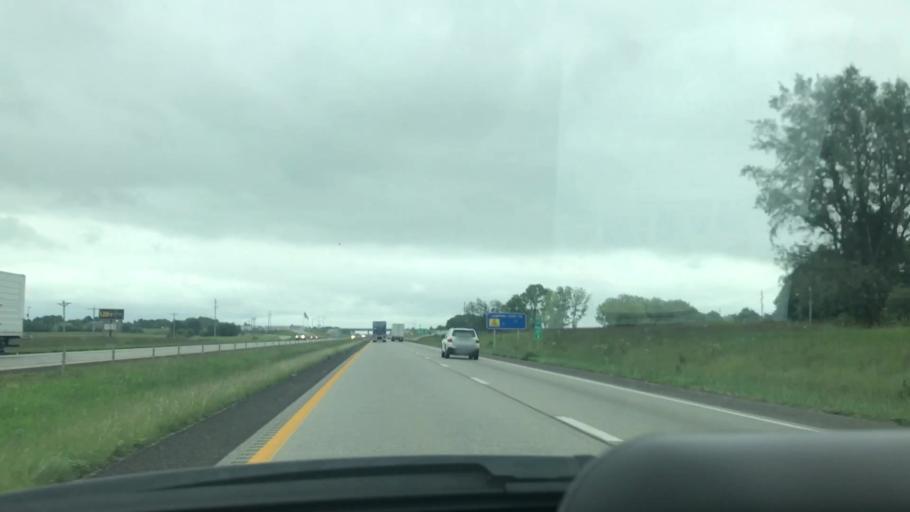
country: US
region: Missouri
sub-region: Greene County
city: Republic
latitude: 37.1989
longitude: -93.4307
